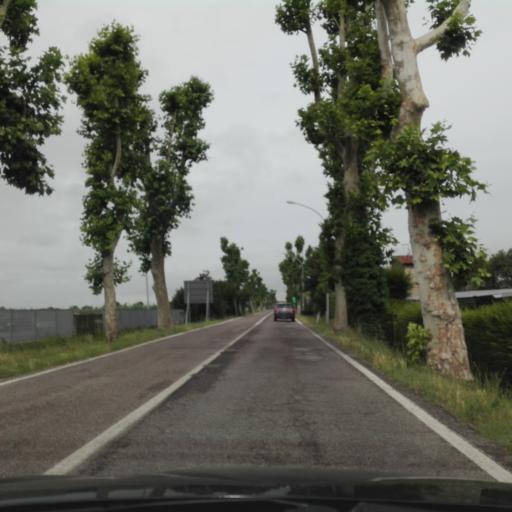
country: IT
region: Veneto
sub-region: Provincia di Rovigo
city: Rovigo
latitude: 45.0774
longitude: 11.7647
